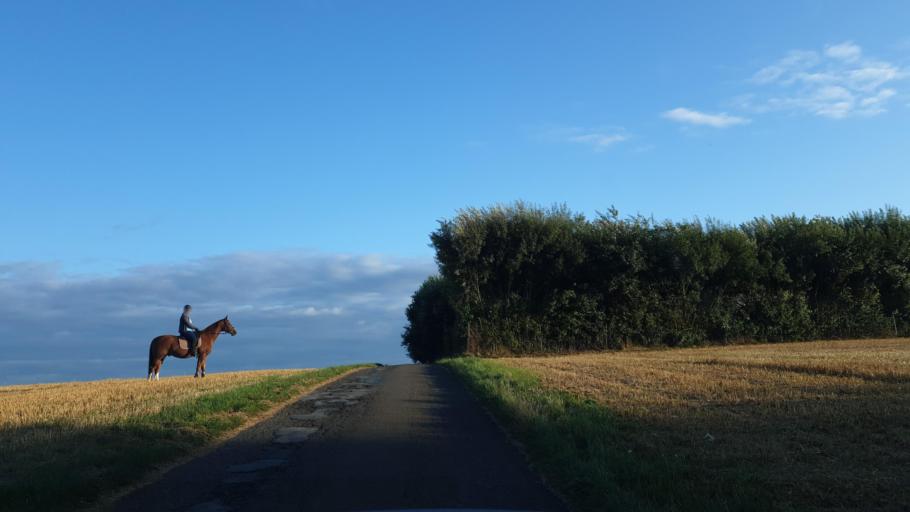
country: DE
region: North Rhine-Westphalia
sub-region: Regierungsbezirk Detmold
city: Huellhorst
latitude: 52.2673
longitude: 8.6889
